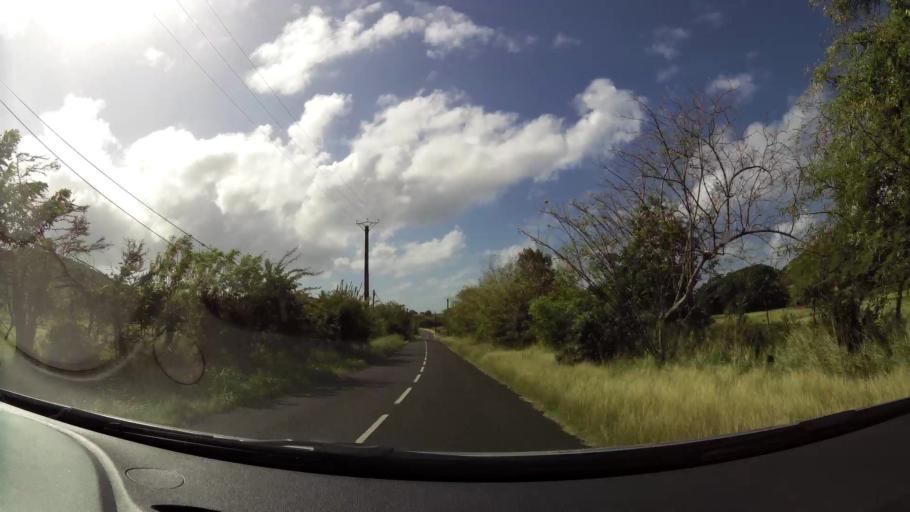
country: MQ
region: Martinique
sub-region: Martinique
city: Le Marin
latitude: 14.4199
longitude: -60.8774
